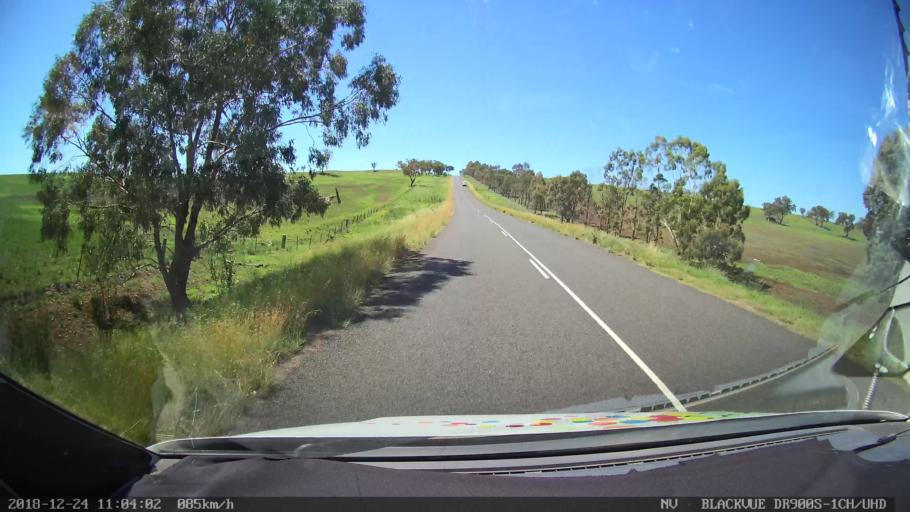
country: AU
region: New South Wales
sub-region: Upper Hunter Shire
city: Merriwa
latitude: -32.1042
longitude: 150.3698
